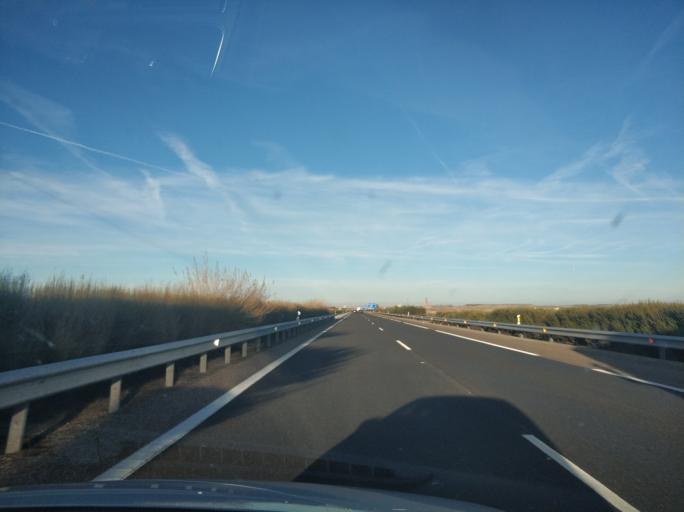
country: ES
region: Castille and Leon
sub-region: Provincia de Valladolid
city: Alaejos
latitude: 41.2885
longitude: -5.2401
